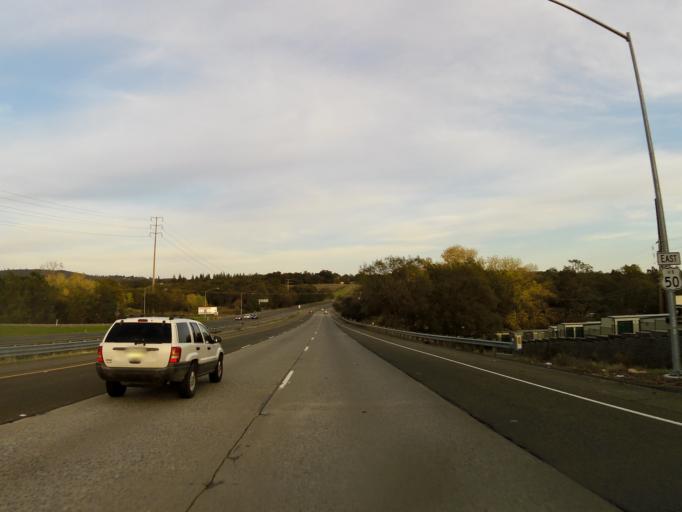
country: US
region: California
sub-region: El Dorado County
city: Cameron Park
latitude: 38.6567
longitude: -120.9969
